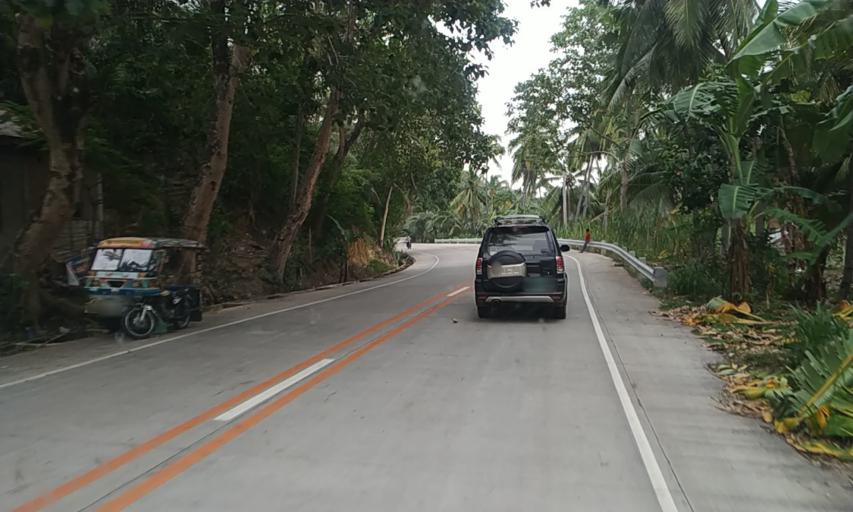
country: PH
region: Central Visayas
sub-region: Province of Negros Oriental
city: Basak
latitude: 10.2062
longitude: 123.3002
